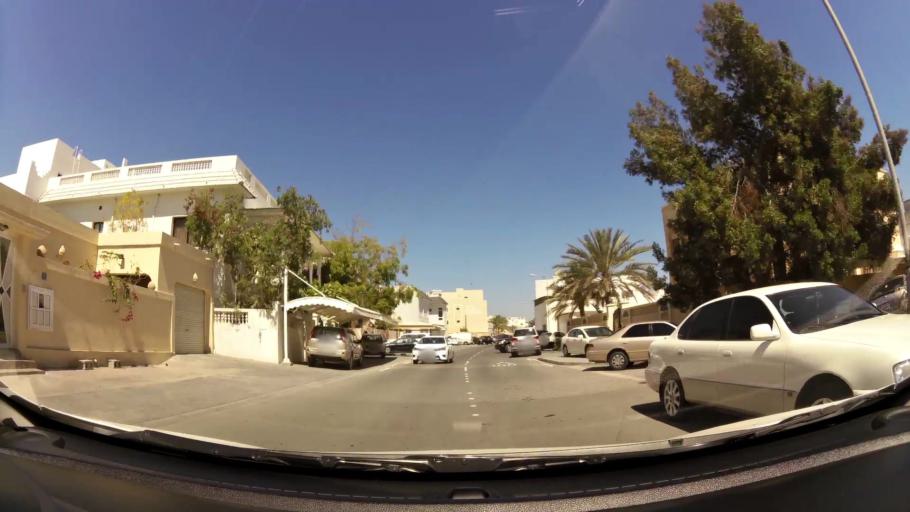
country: BH
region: Muharraq
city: Al Muharraq
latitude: 26.2690
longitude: 50.6058
